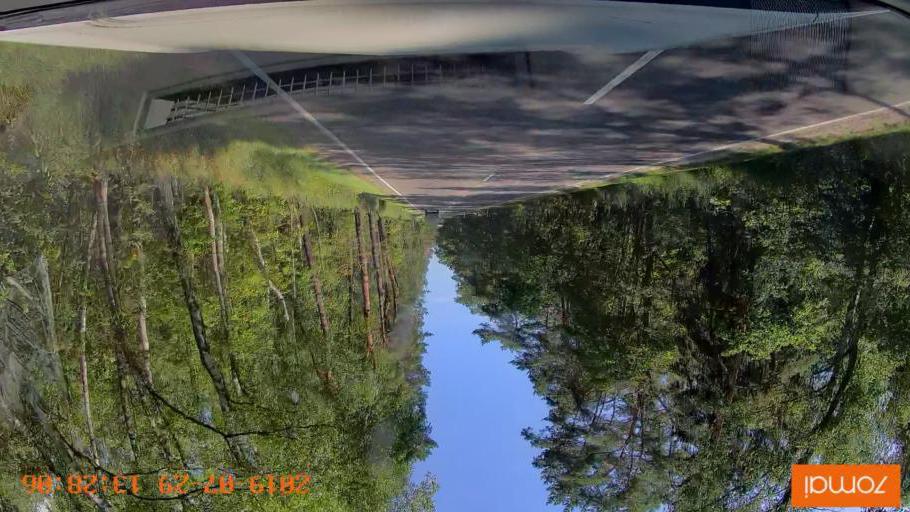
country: RU
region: Kaliningrad
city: Vzmorye
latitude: 54.7047
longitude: 20.2880
